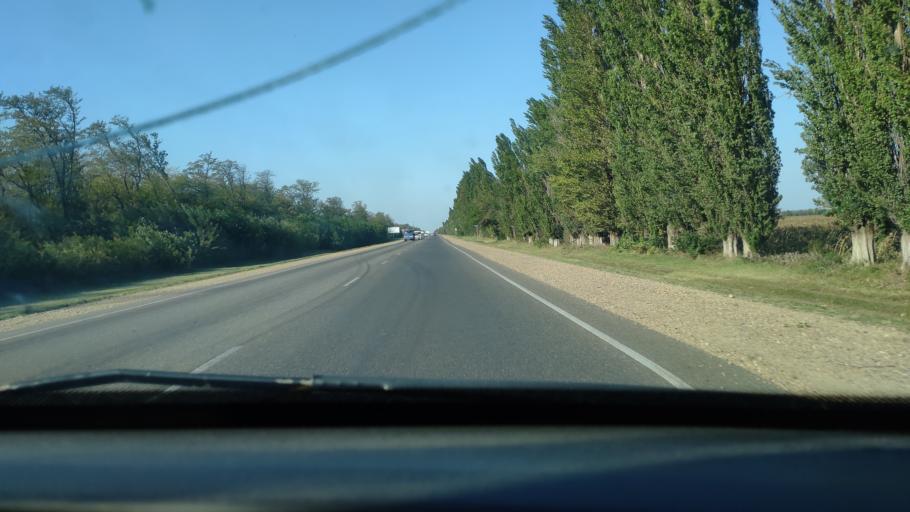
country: RU
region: Krasnodarskiy
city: Novotitarovskaya
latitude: 45.2700
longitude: 39.0040
